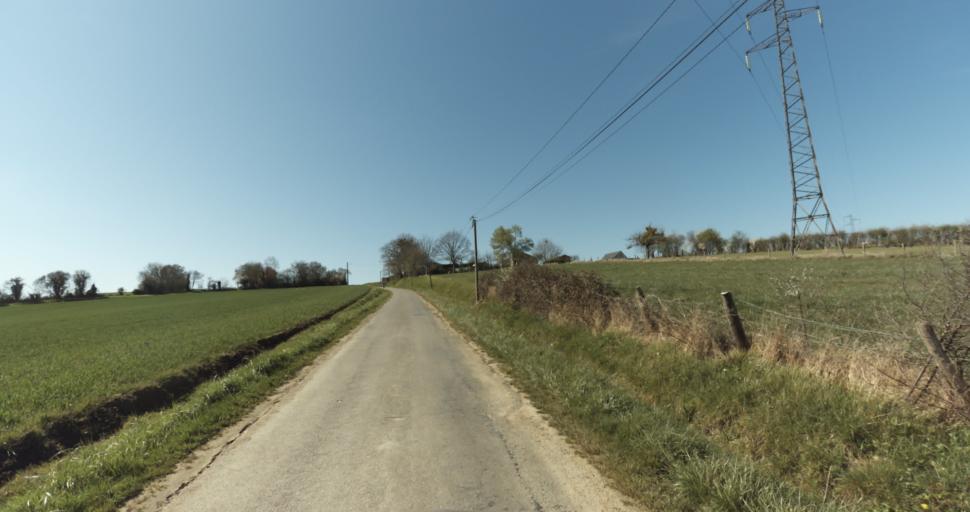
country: FR
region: Lower Normandy
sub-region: Departement du Calvados
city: Saint-Pierre-sur-Dives
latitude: 49.0543
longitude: -0.0108
